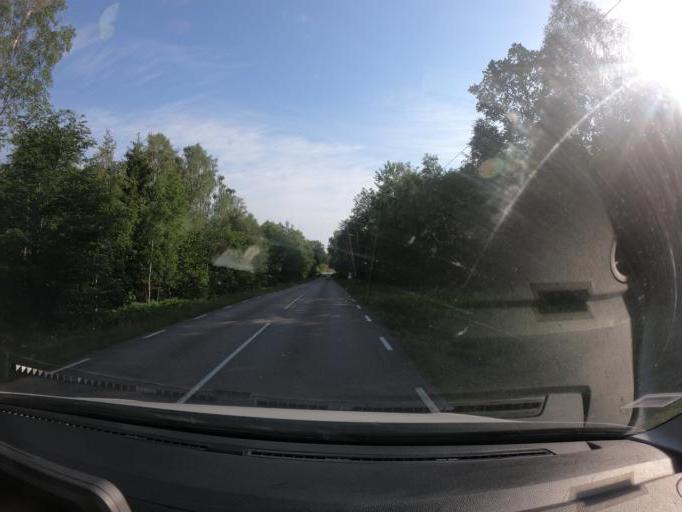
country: SE
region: Skane
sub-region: Orkelljunga Kommun
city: OErkelljunga
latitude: 56.3014
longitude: 13.3879
